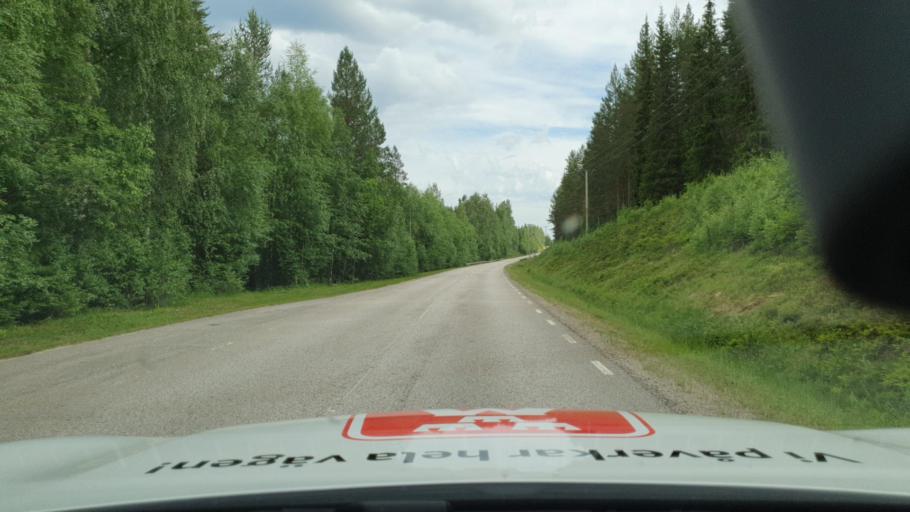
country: NO
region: Hedmark
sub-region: Trysil
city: Innbygda
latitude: 61.0096
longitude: 12.4808
